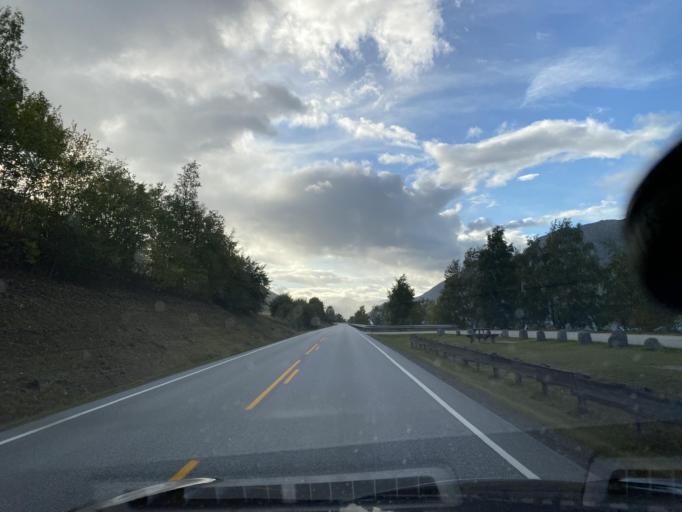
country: NO
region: Oppland
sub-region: Vaga
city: Vagamo
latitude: 61.8481
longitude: 8.9531
